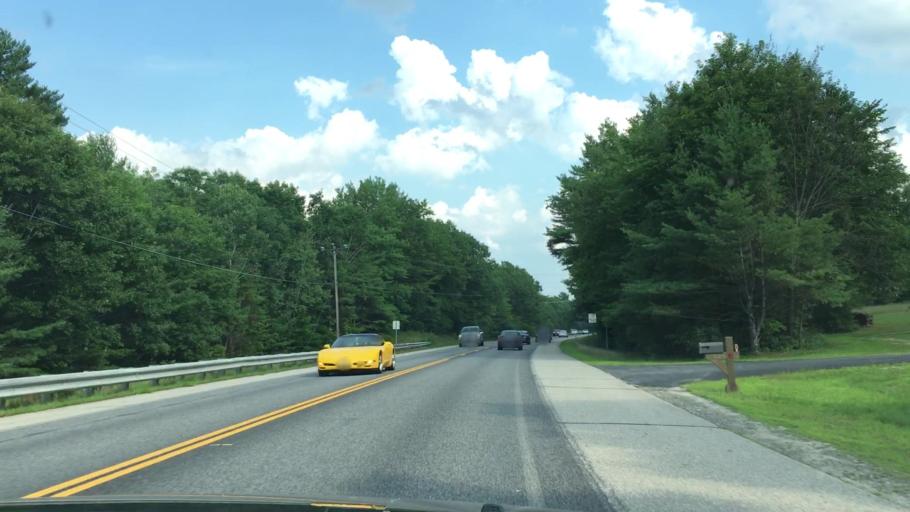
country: US
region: New Hampshire
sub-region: Strafford County
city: Farmington
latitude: 43.3835
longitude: -71.0723
